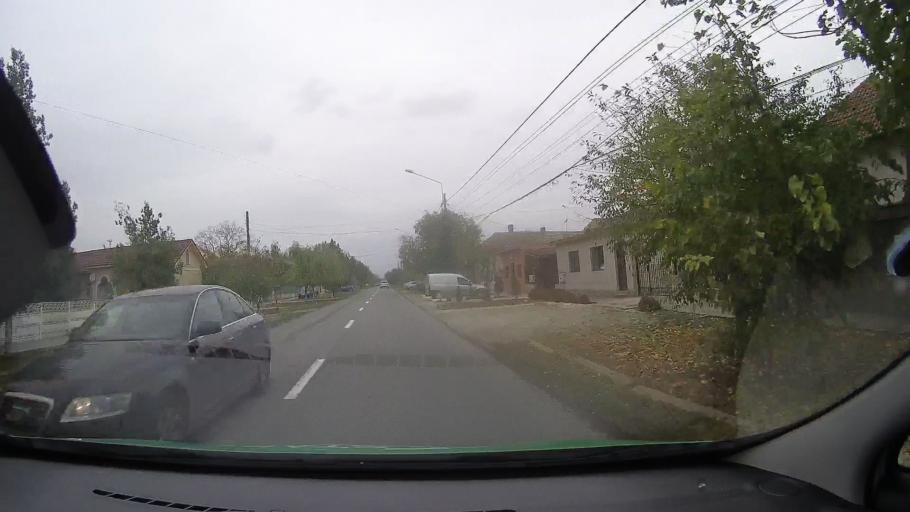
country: RO
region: Constanta
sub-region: Comuna Mihail Kogalniceanu
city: Mihail Kogalniceanu
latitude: 44.3713
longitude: 28.4636
